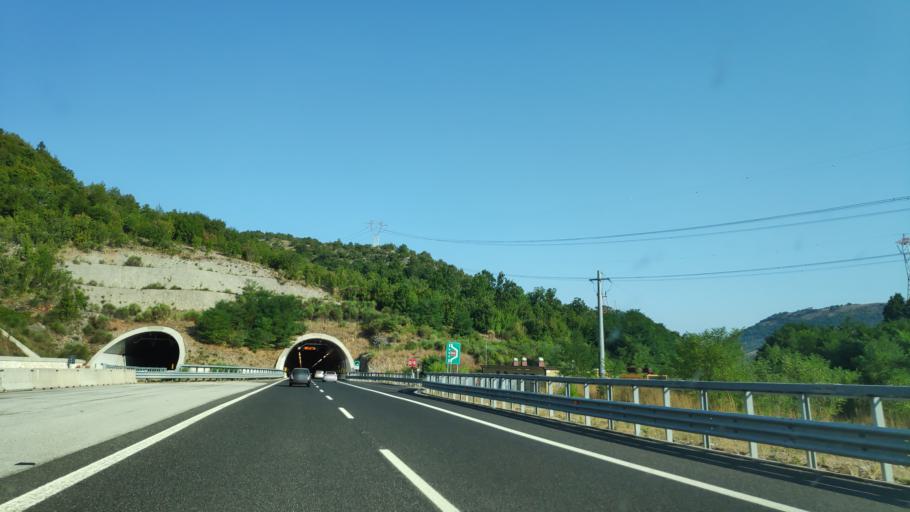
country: IT
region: Campania
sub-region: Provincia di Salerno
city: Casalbuono
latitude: 40.2004
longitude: 15.6873
